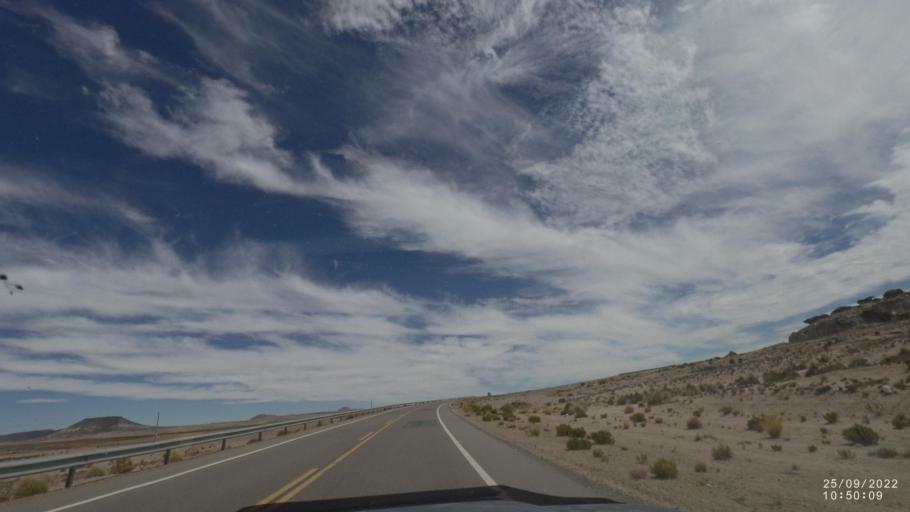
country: BO
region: Oruro
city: Challapata
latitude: -19.5798
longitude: -66.8347
